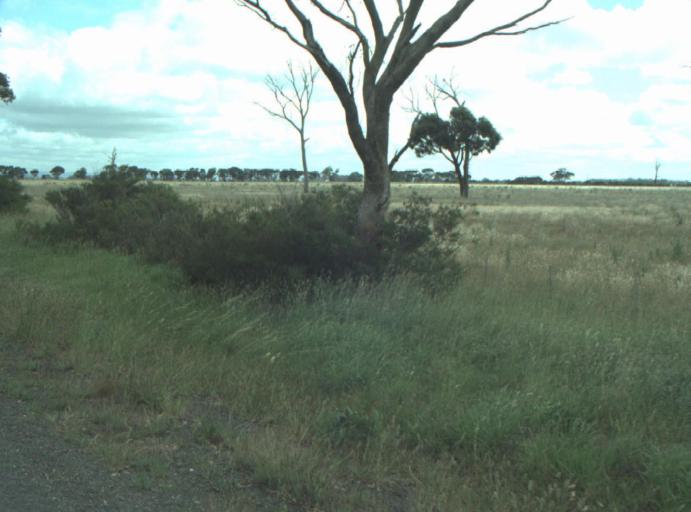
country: AU
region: Victoria
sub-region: Greater Geelong
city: Lara
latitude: -37.8782
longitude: 144.3501
